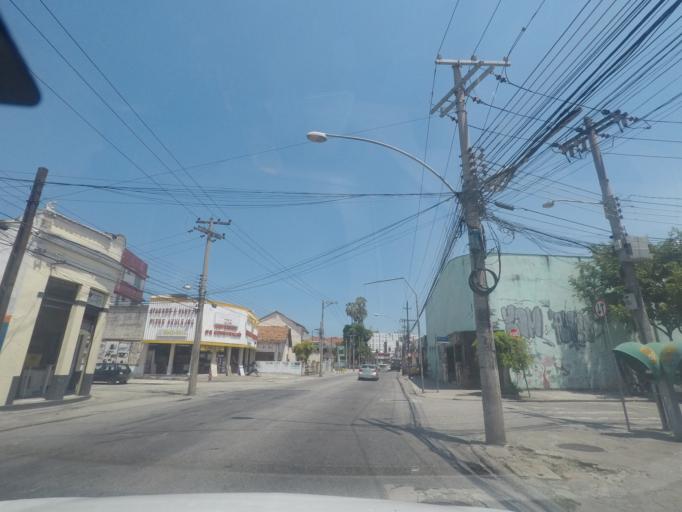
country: BR
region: Rio de Janeiro
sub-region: Rio De Janeiro
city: Rio de Janeiro
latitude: -22.8506
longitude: -43.2649
